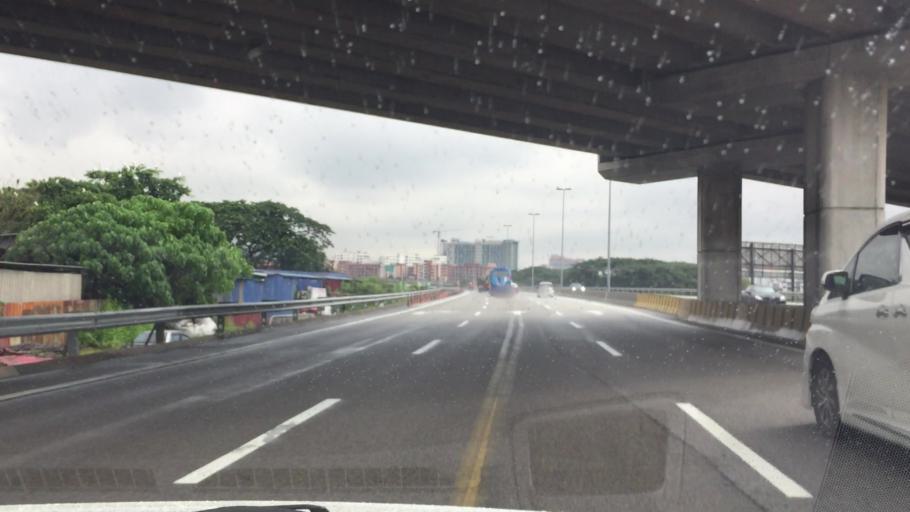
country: MY
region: Kuala Lumpur
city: Kuala Lumpur
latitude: 3.1145
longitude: 101.7139
